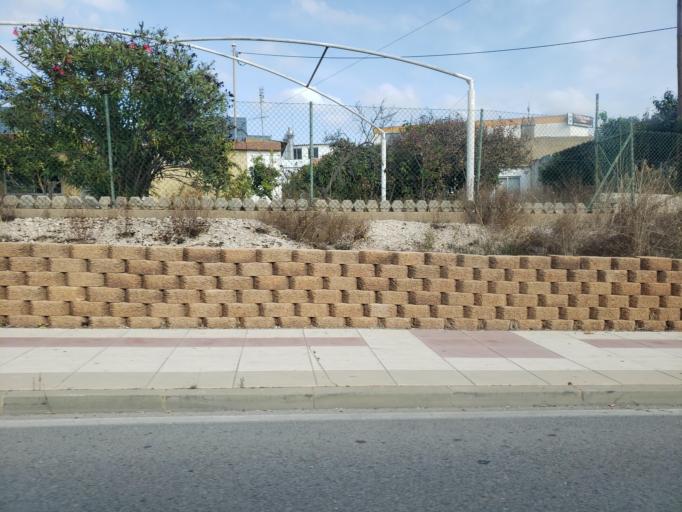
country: PT
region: Faro
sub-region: Portimao
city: Portimao
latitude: 37.1501
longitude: -8.5503
